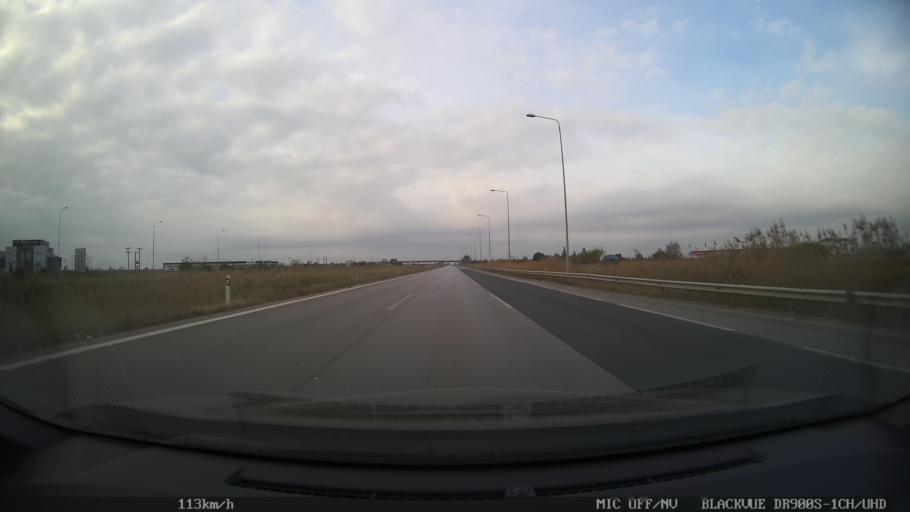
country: GR
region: Central Macedonia
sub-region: Nomos Thessalonikis
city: Sindos
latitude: 40.6472
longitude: 22.8068
